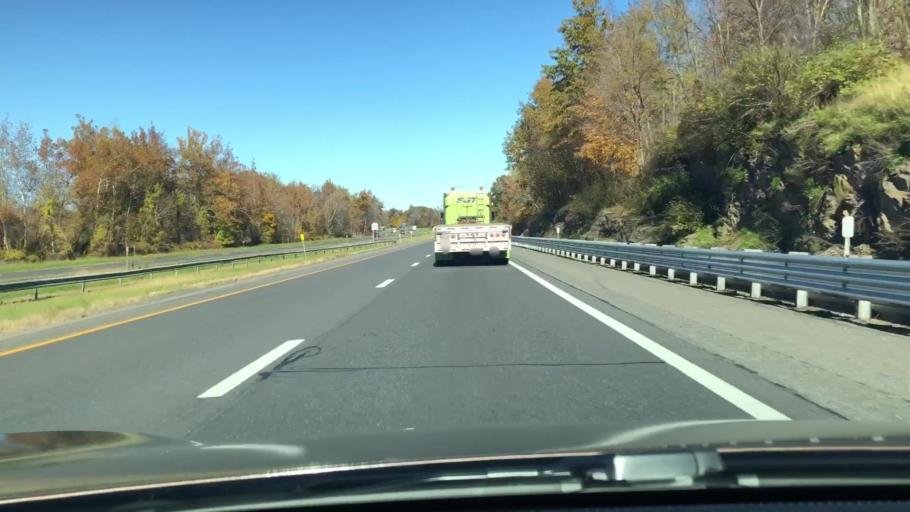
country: US
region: New York
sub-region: Ulster County
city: Lake Katrine
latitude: 42.0262
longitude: -73.9952
